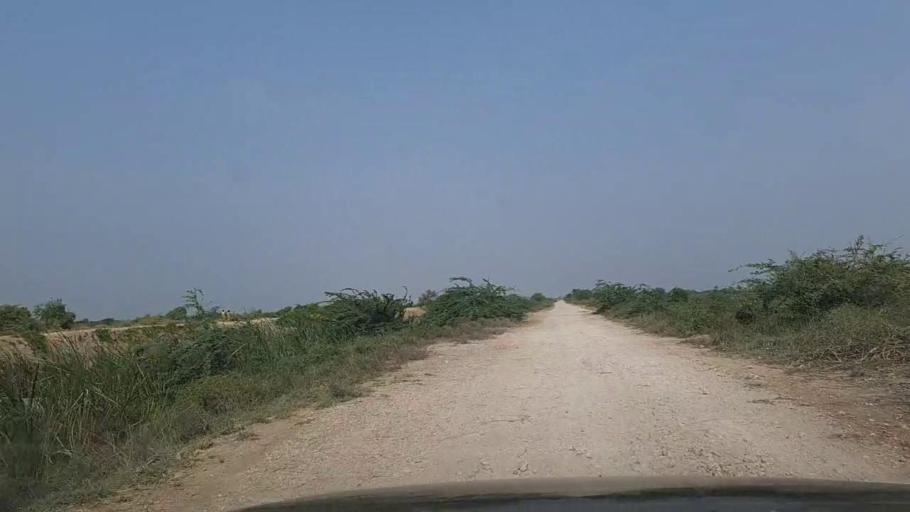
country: PK
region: Sindh
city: Thatta
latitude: 24.7435
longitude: 67.8065
